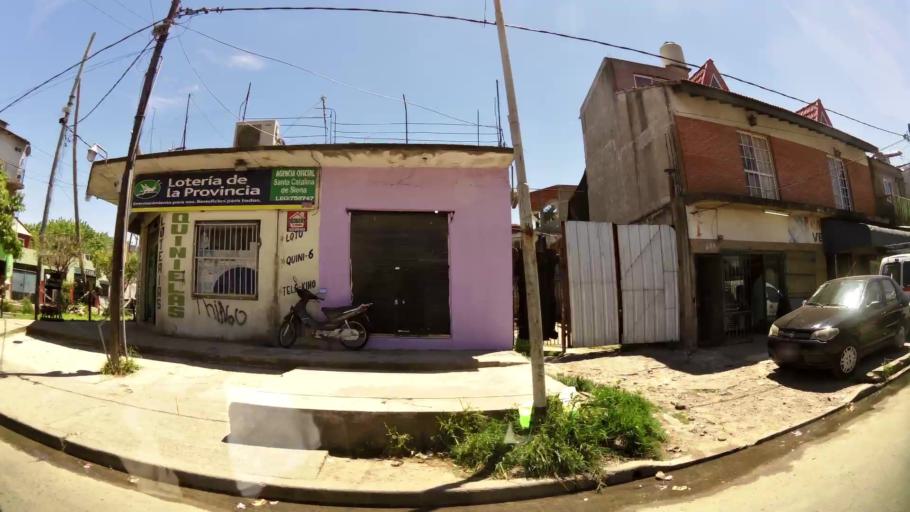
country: AR
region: Buenos Aires
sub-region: Partido de Quilmes
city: Quilmes
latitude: -34.7144
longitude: -58.3202
